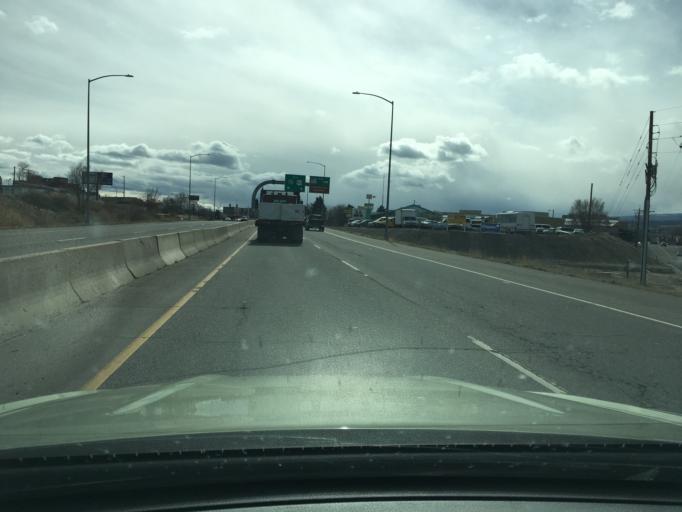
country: US
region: Colorado
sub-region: Mesa County
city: Grand Junction
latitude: 39.0730
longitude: -108.5732
